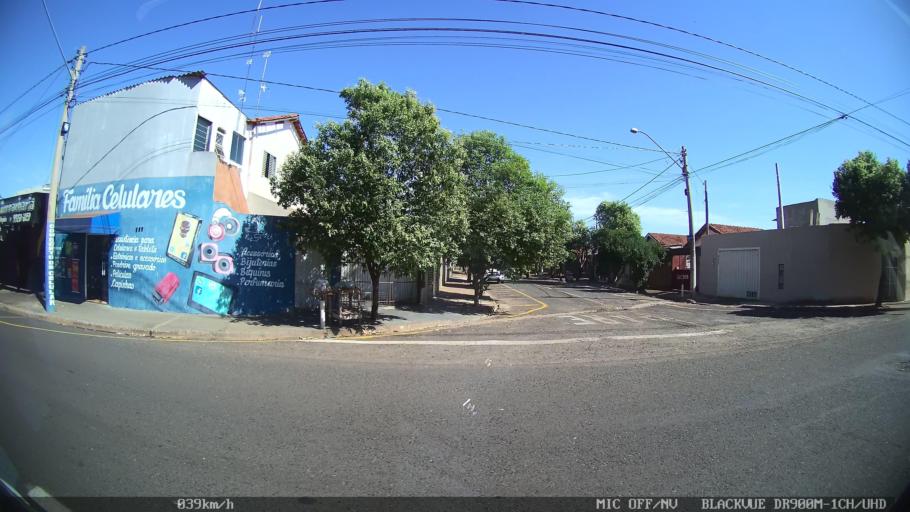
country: BR
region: Sao Paulo
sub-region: Sao Jose Do Rio Preto
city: Sao Jose do Rio Preto
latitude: -20.7485
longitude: -49.4076
